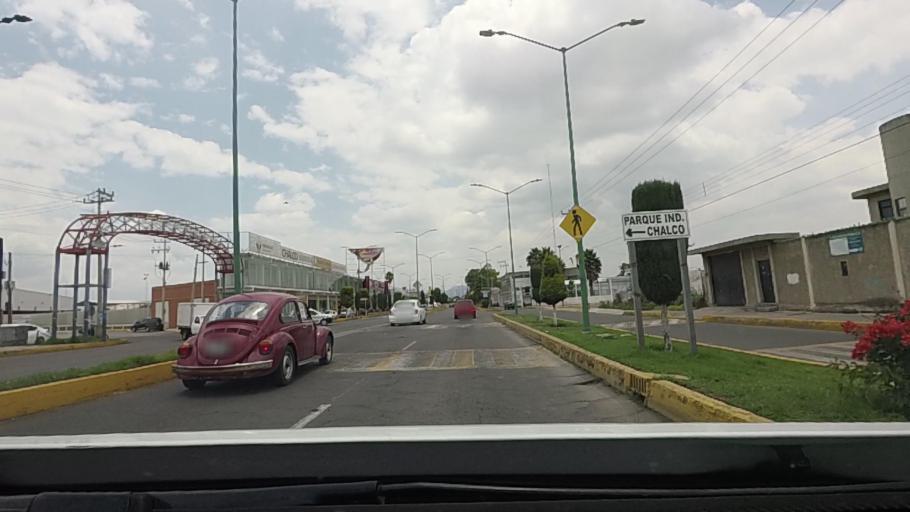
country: MX
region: Mexico
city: Chalco de Diaz Covarrubias
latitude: 19.2563
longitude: -98.8878
